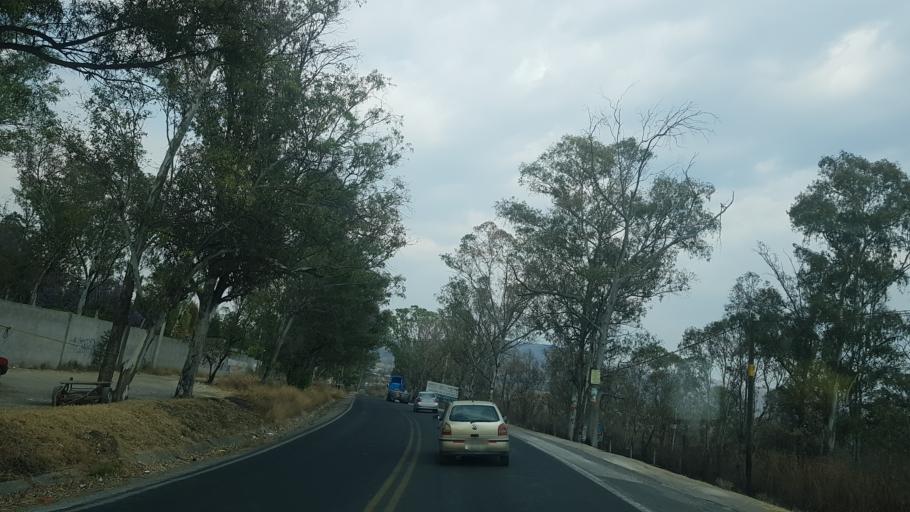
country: MX
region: Puebla
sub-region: Santa Isabel Cholula
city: Santa Ana Acozautla
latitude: 18.9446
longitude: -98.3916
